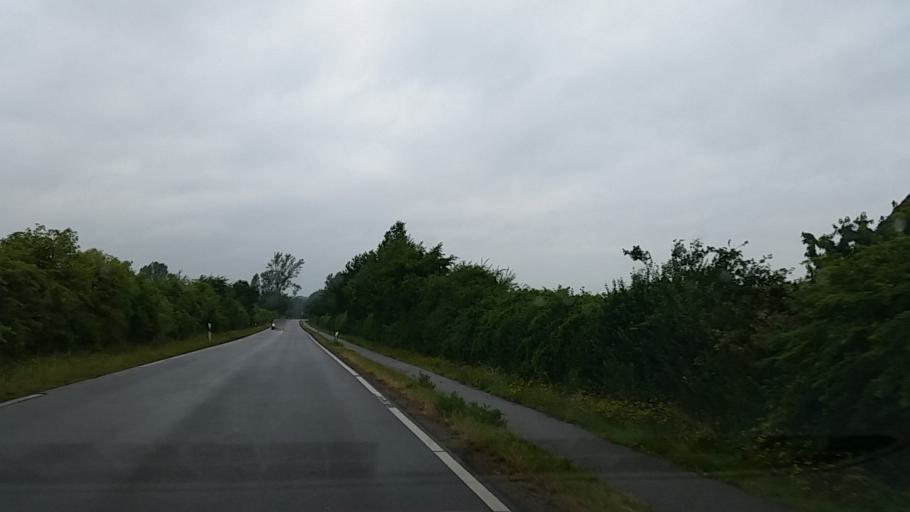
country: DE
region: Mecklenburg-Vorpommern
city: Lambrechtshagen
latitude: 54.1170
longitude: 12.0340
